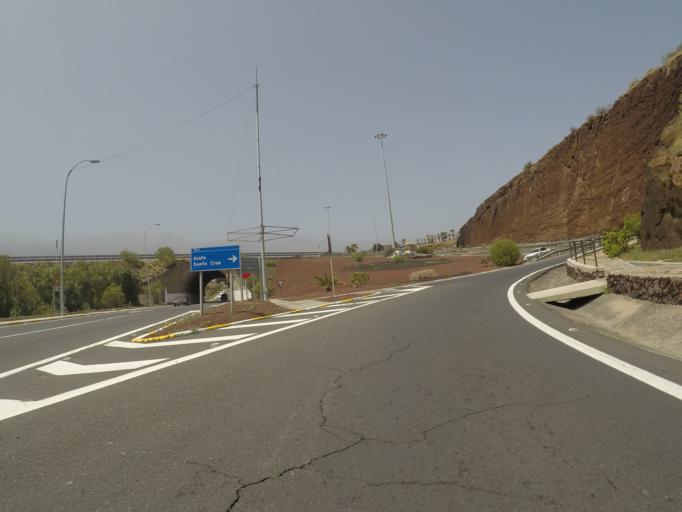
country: ES
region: Canary Islands
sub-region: Provincia de Santa Cruz de Tenerife
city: Guimar
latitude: 28.3042
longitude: -16.3824
